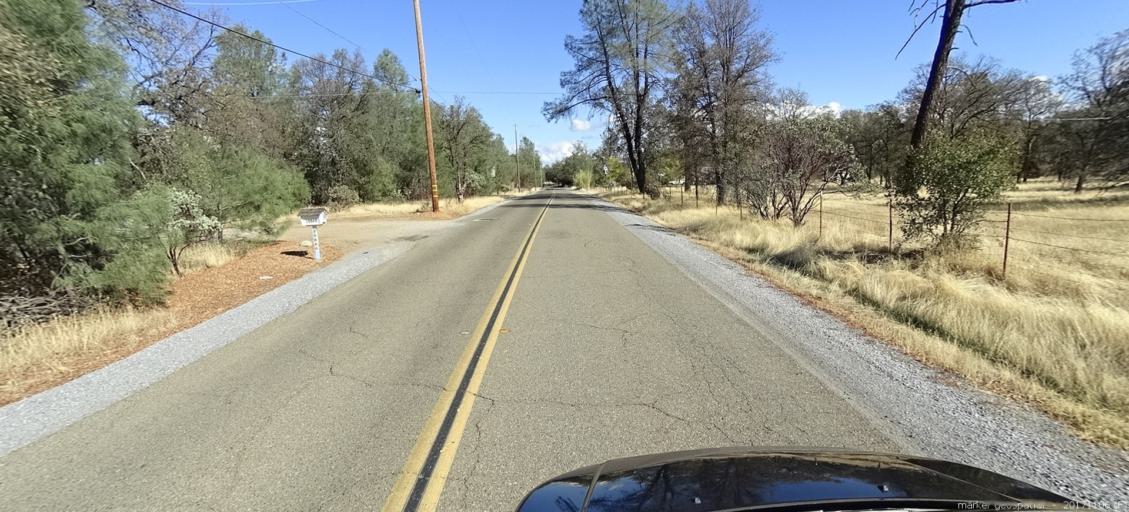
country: US
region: California
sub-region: Shasta County
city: Palo Cedro
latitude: 40.6015
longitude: -122.2820
